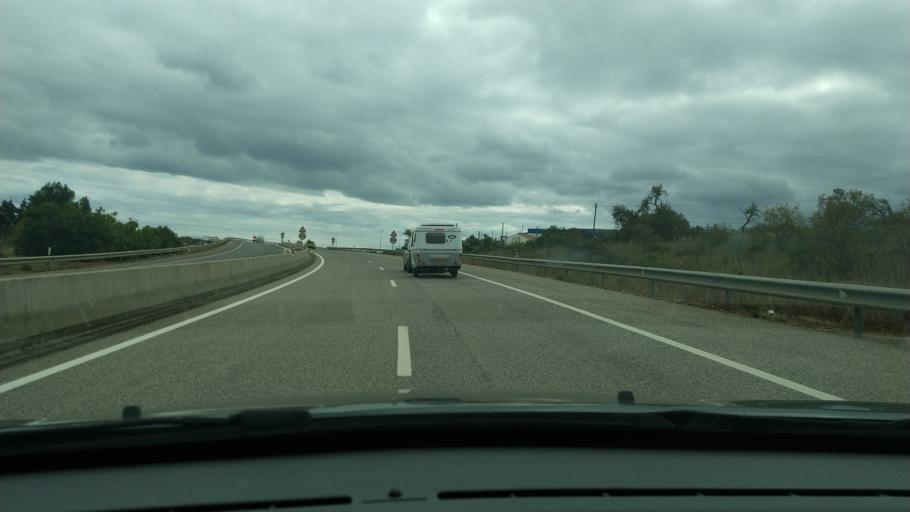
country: PT
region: Faro
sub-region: Lagos
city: Lagos
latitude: 37.1048
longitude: -8.6963
